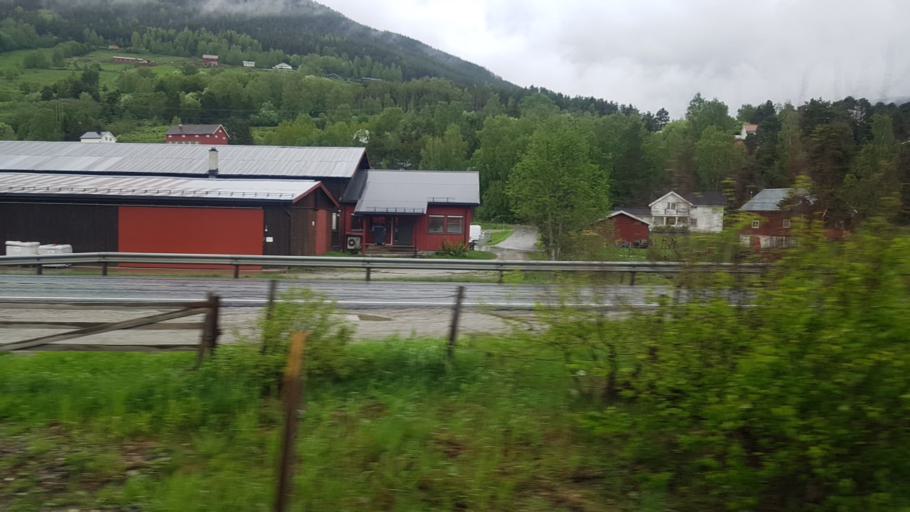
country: NO
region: Oppland
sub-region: Sor-Fron
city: Hundorp
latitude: 61.5453
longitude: 10.0224
